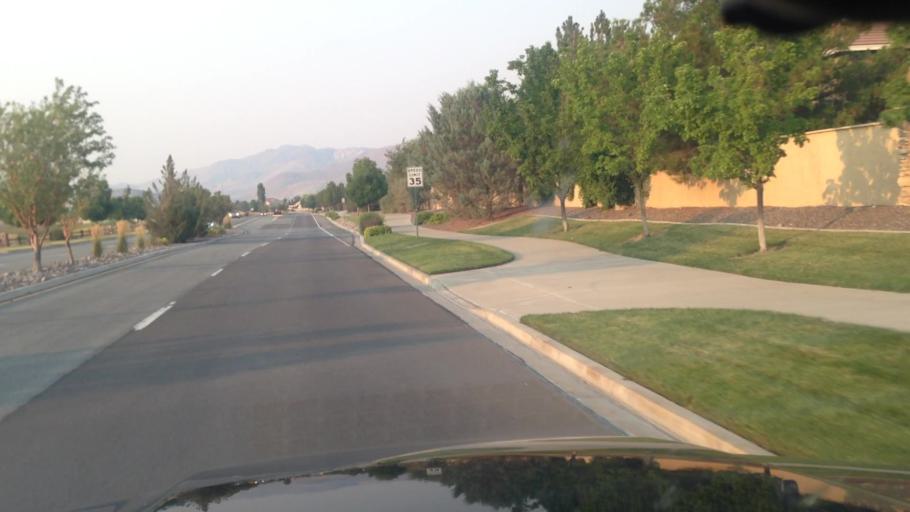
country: US
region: Nevada
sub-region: Washoe County
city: Sparks
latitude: 39.4441
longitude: -119.7450
